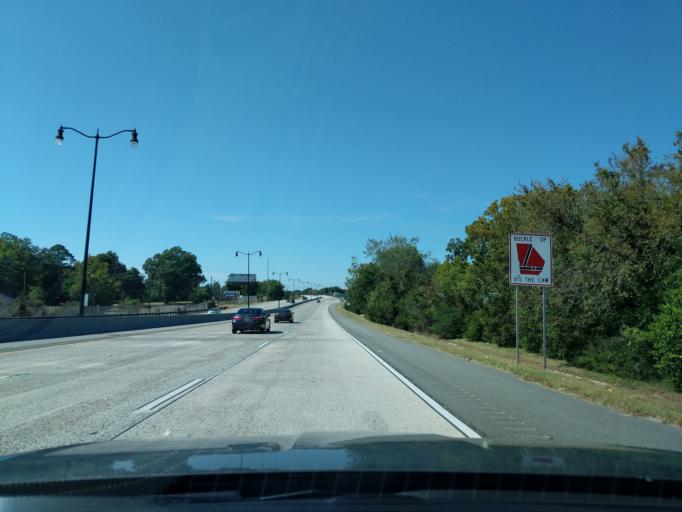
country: US
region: Georgia
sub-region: Richmond County
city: Augusta
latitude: 33.4800
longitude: -81.9884
